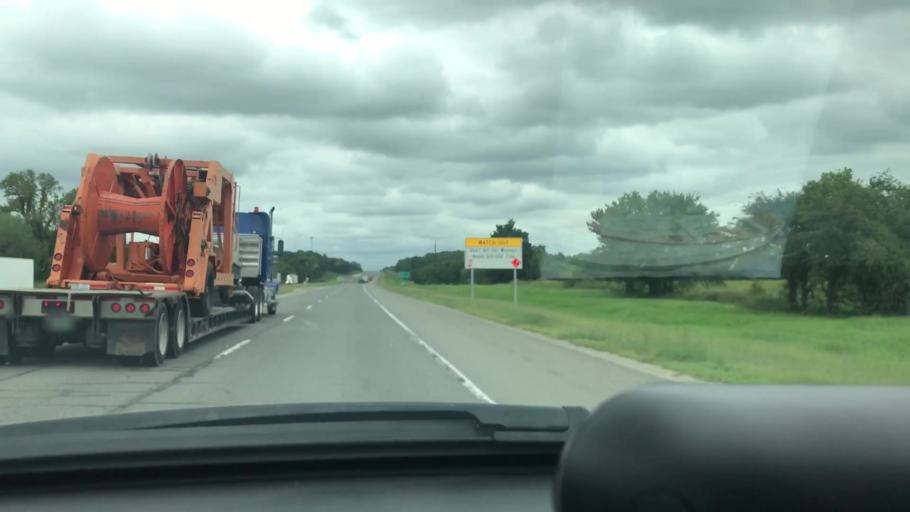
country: US
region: Oklahoma
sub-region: Muskogee County
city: Muskogee
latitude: 35.8144
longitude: -95.4025
